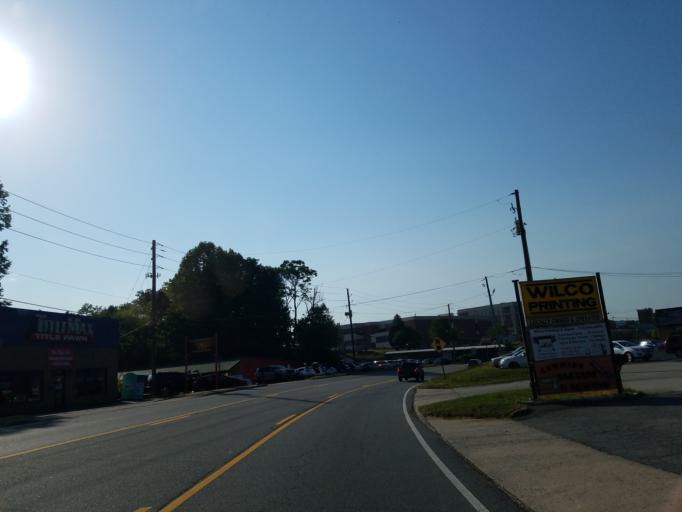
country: US
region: Georgia
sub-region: Forsyth County
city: Cumming
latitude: 34.2036
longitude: -84.1365
